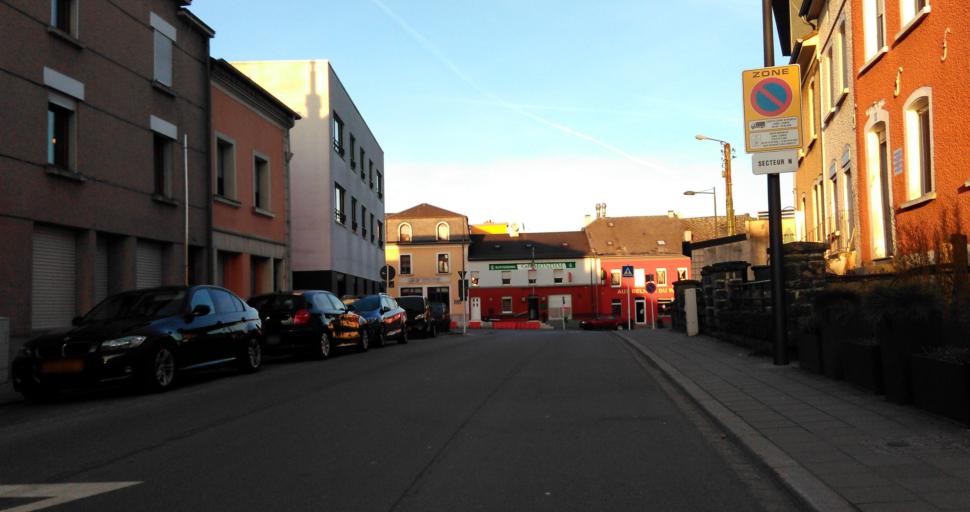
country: LU
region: Luxembourg
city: Rodange
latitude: 49.5451
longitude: 5.8382
